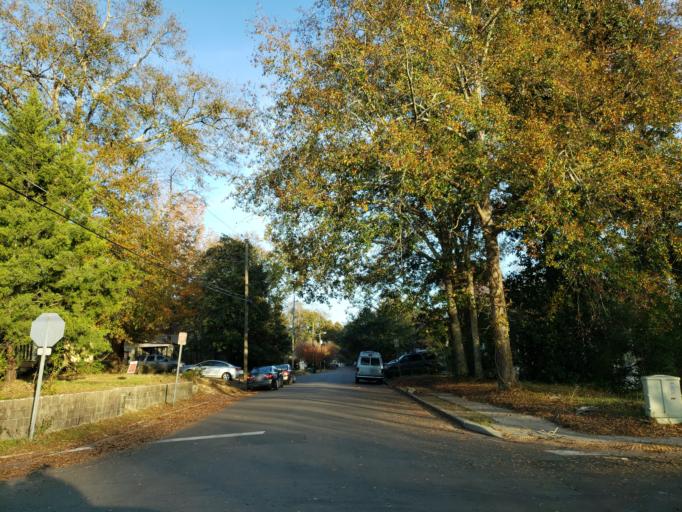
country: US
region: Mississippi
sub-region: Forrest County
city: Hattiesburg
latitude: 31.3302
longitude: -89.3004
